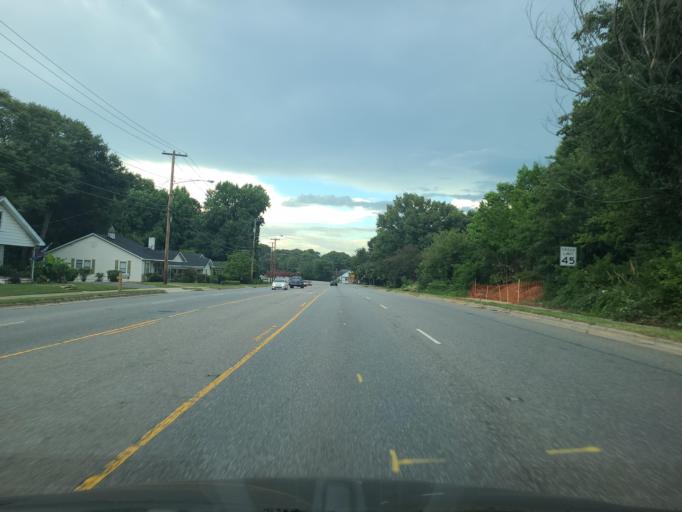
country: US
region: North Carolina
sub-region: Gaston County
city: Ranlo
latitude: 35.2837
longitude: -81.1491
